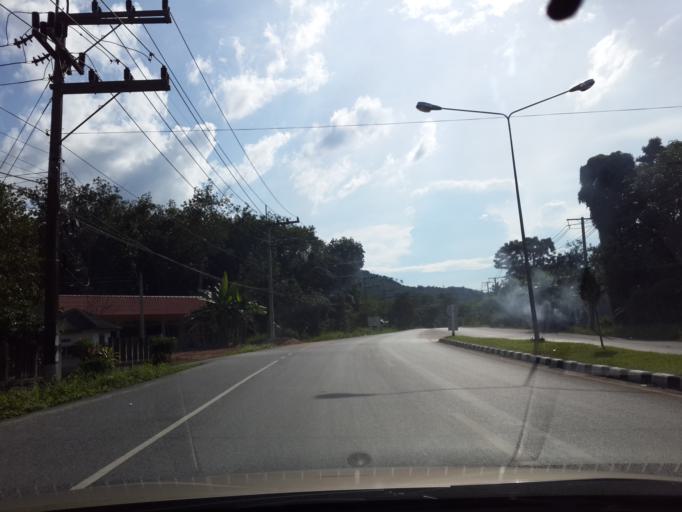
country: TH
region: Yala
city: Yala
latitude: 6.5004
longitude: 101.2867
